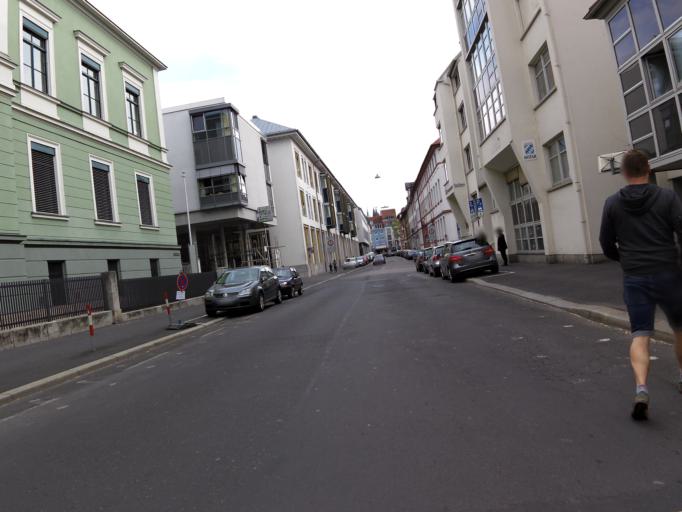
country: DE
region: Bavaria
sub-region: Regierungsbezirk Unterfranken
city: Wuerzburg
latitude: 49.7990
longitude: 9.9293
